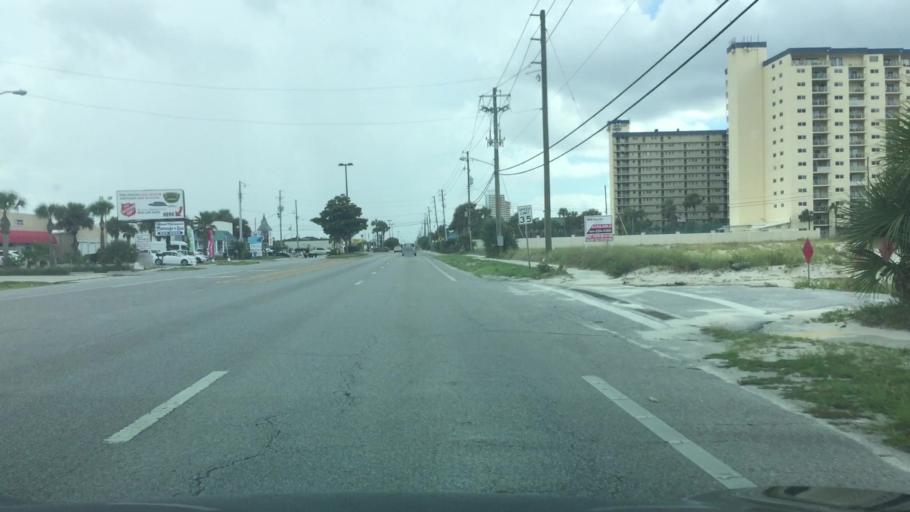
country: US
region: Florida
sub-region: Bay County
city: Lower Grand Lagoon
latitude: 30.1490
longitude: -85.7626
